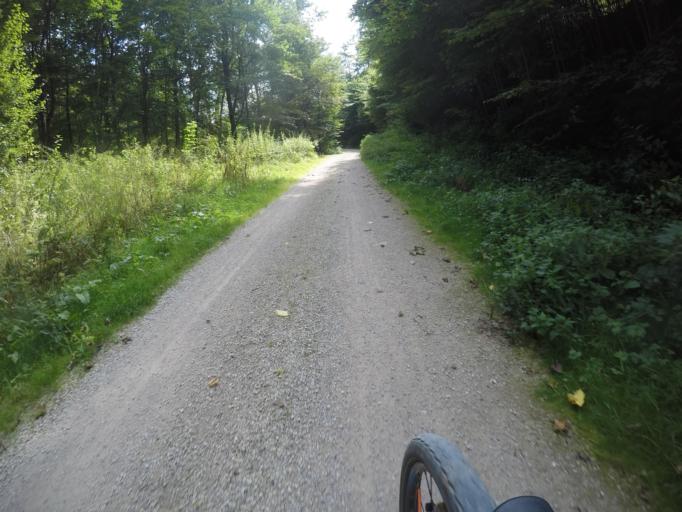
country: DE
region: Baden-Wuerttemberg
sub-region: Tuebingen Region
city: Bad Urach
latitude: 48.4750
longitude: 9.4064
